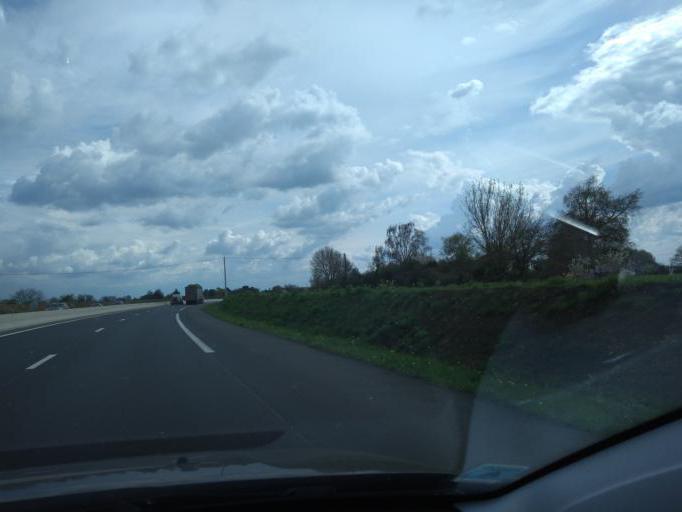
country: FR
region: Pays de la Loire
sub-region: Departement de Maine-et-Loire
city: Grez-Neuville
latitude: 47.6037
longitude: -0.7054
